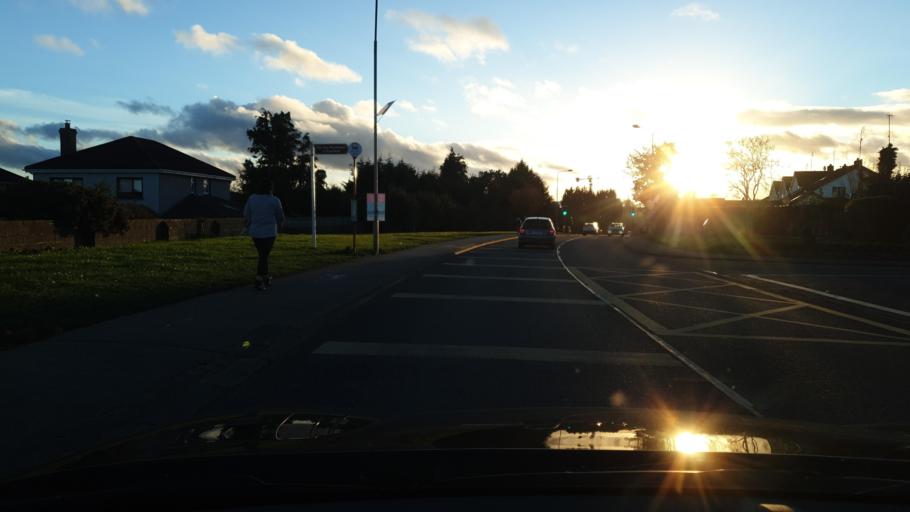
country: IE
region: Leinster
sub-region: Lu
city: Drogheda
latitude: 53.7241
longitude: -6.3327
